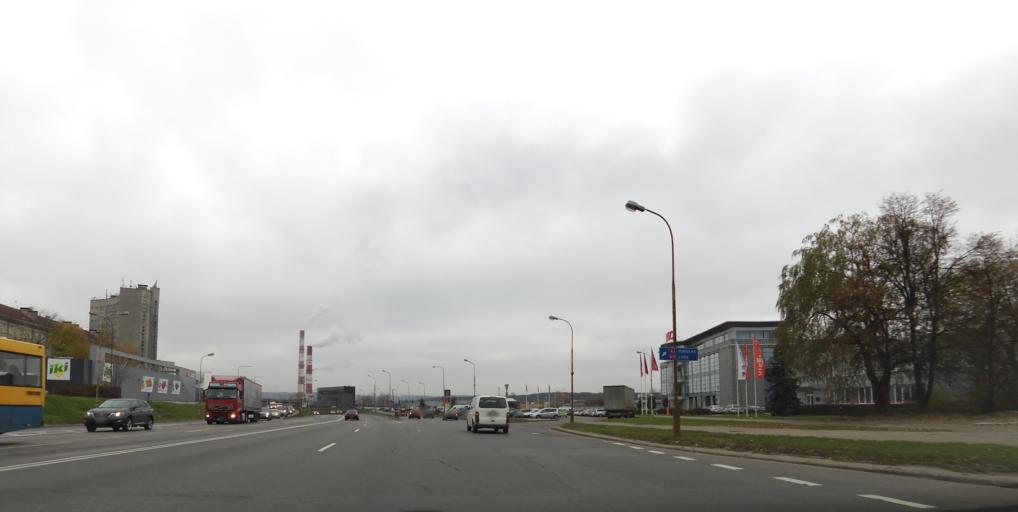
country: LT
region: Vilnius County
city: Vilkpede
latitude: 54.6727
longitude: 25.2394
